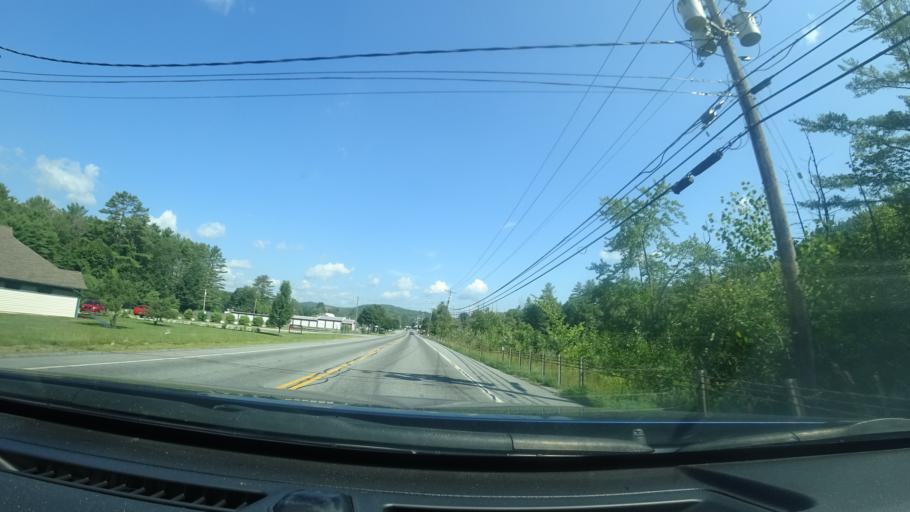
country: US
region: New York
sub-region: Warren County
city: Warrensburg
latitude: 43.6439
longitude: -73.7993
